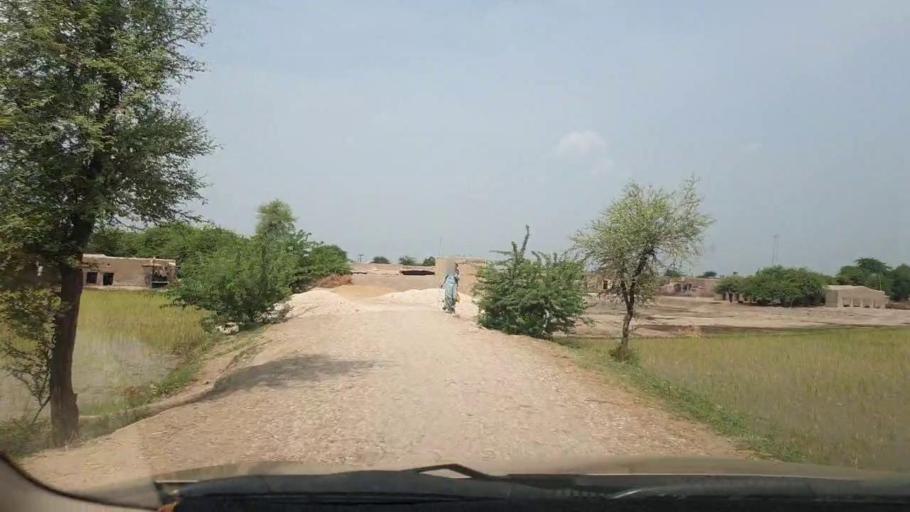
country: PK
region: Sindh
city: Larkana
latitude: 27.5094
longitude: 68.1342
